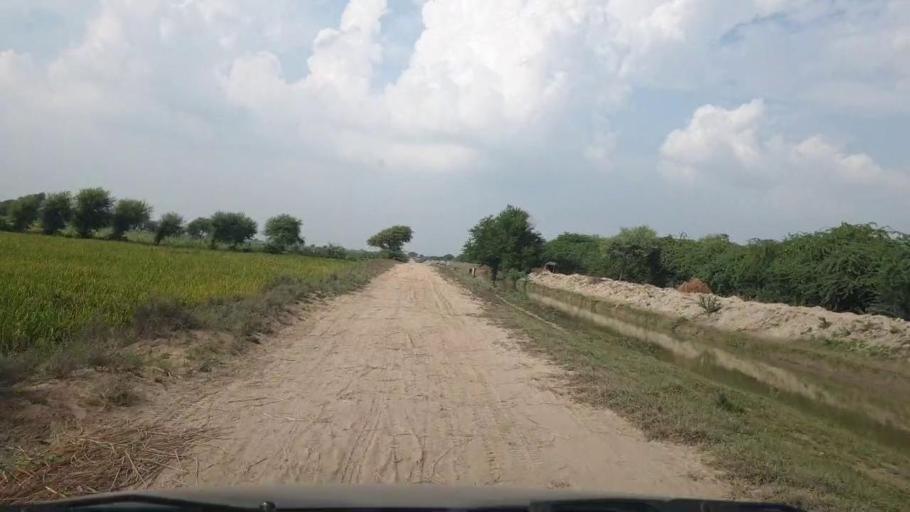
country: PK
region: Sindh
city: Badin
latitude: 24.5665
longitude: 68.6357
